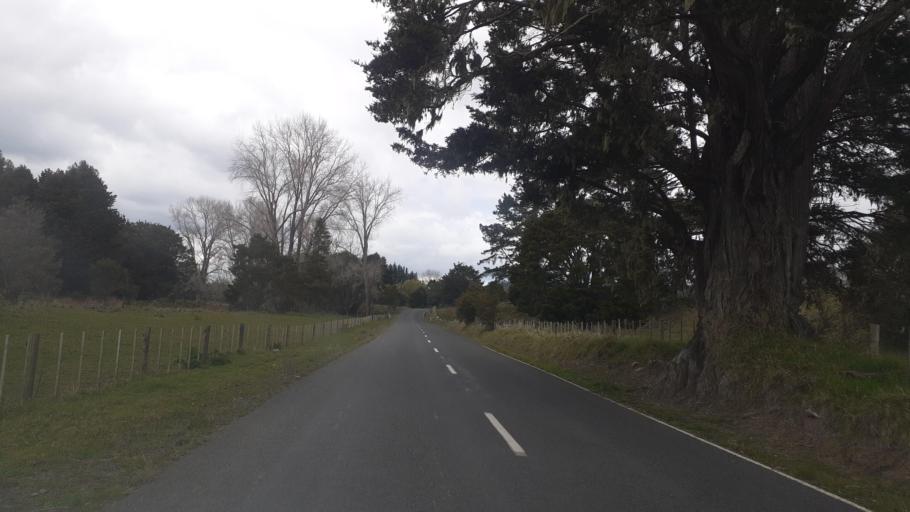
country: NZ
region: Northland
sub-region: Far North District
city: Moerewa
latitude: -35.5819
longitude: 173.9722
